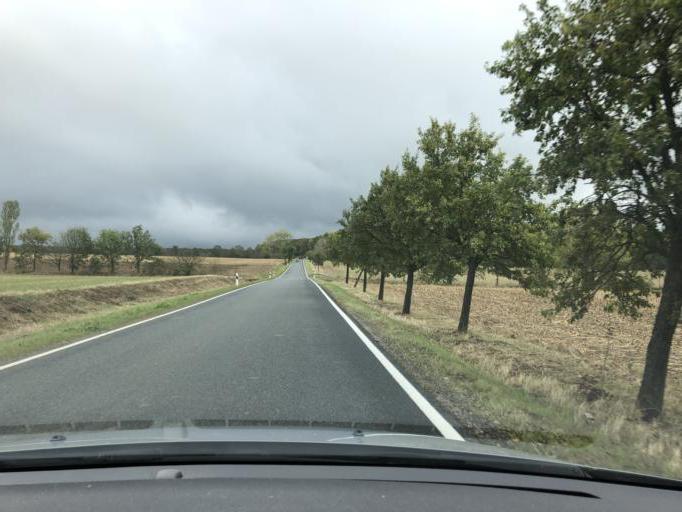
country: DE
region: Thuringia
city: Anrode
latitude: 51.2638
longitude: 10.3530
